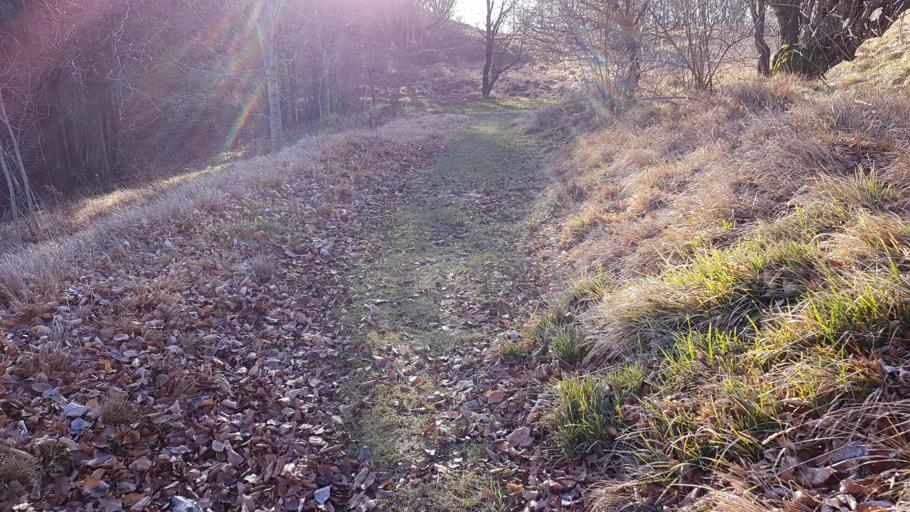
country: IT
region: Liguria
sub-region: Provincia di Genova
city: Torriglia
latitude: 44.5463
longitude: 9.1506
